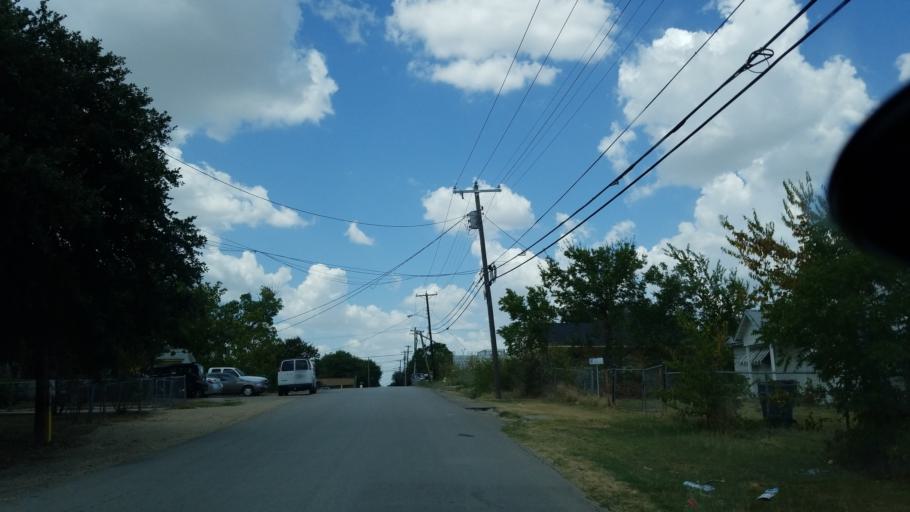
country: US
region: Texas
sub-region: Dallas County
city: Cockrell Hill
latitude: 32.7482
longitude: -96.9127
